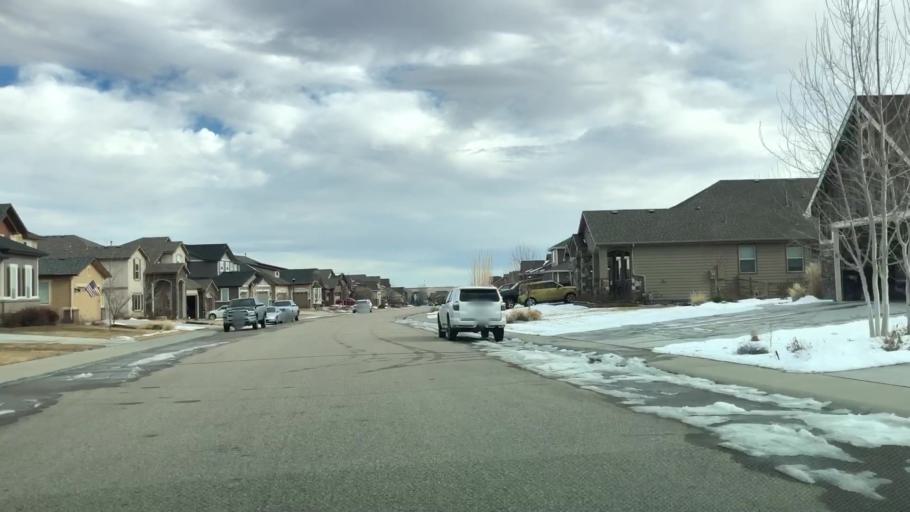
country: US
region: Colorado
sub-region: Weld County
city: Windsor
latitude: 40.4510
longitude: -104.9556
